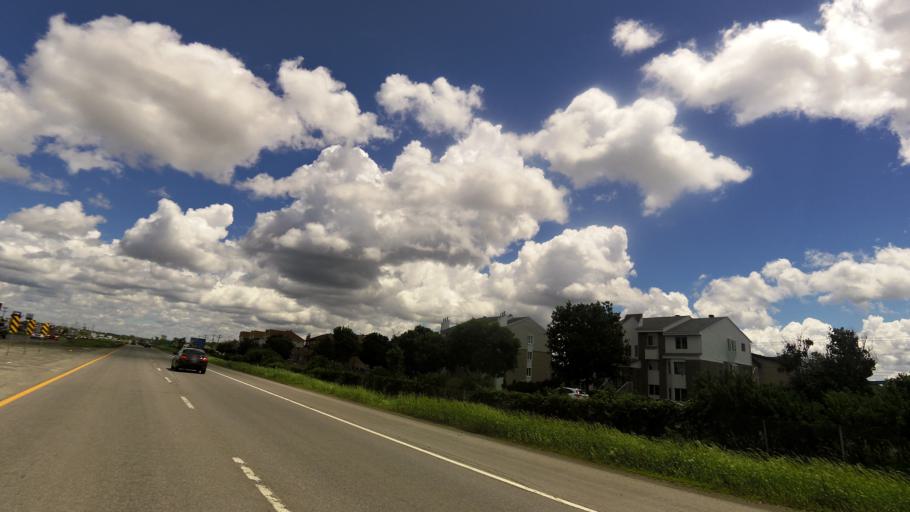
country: CA
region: Quebec
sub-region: Laurentides
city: Saint-Eustache
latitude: 45.5735
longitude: -73.8979
